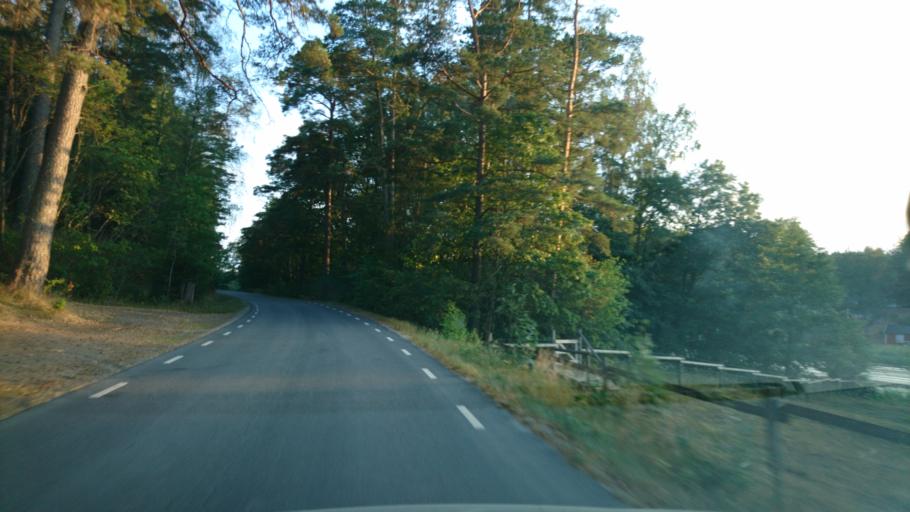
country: SE
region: Uppsala
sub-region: Uppsala Kommun
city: Saevja
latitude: 59.7903
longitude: 17.6664
